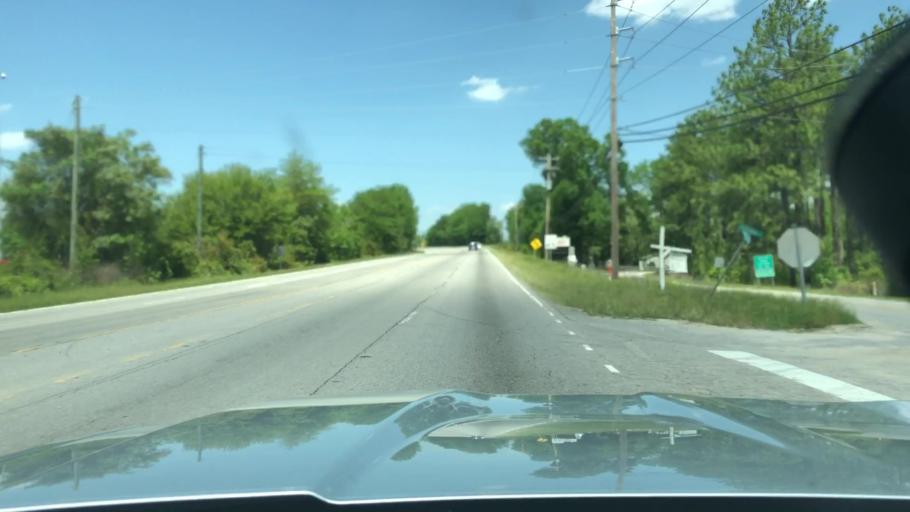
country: US
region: South Carolina
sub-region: Lexington County
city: Pineridge
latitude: 33.9056
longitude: -81.0656
